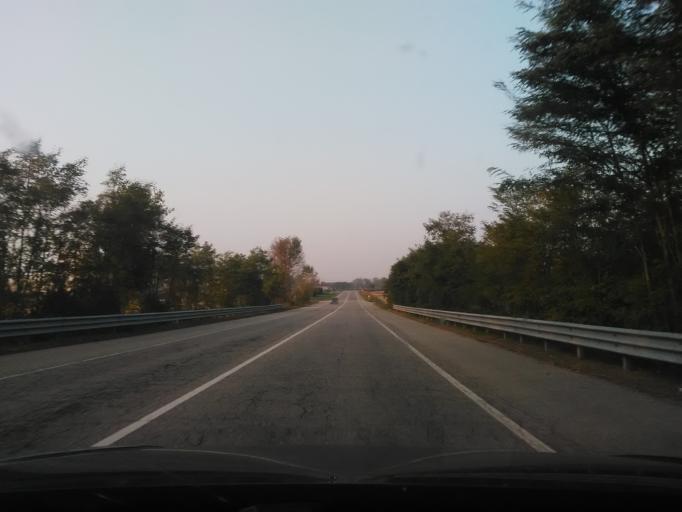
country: IT
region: Piedmont
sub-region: Provincia di Vercelli
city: Stroppiana
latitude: 45.2512
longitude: 8.4606
